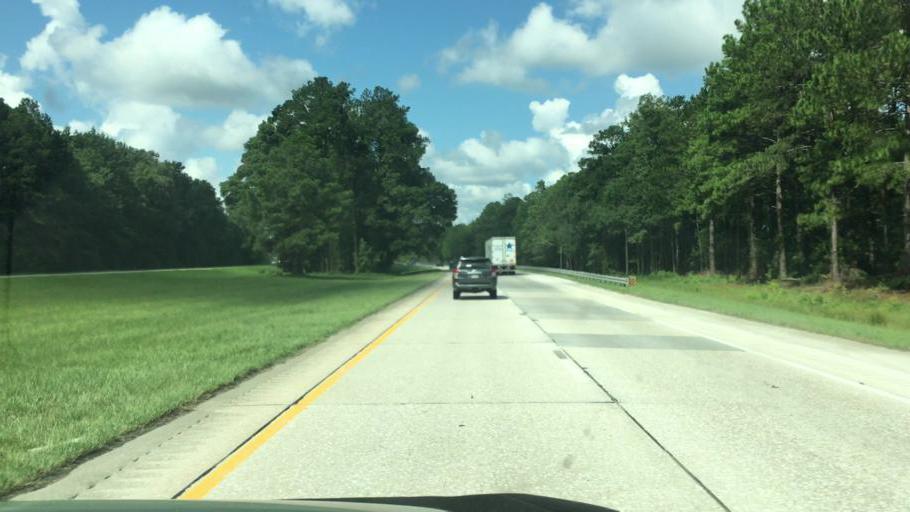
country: US
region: South Carolina
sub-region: Dillon County
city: Latta
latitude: 34.4043
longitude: -79.4425
